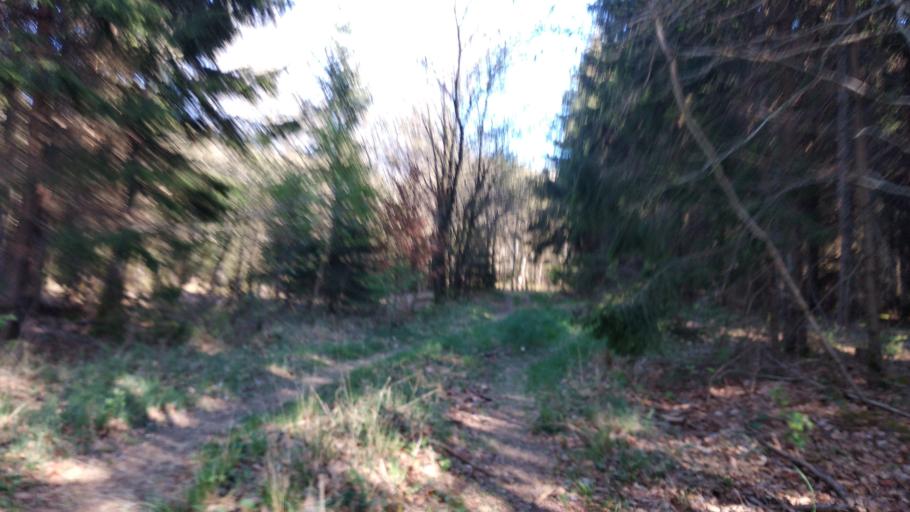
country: DE
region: Bavaria
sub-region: Upper Bavaria
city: Grasbrunn
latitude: 48.0952
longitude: 11.7491
